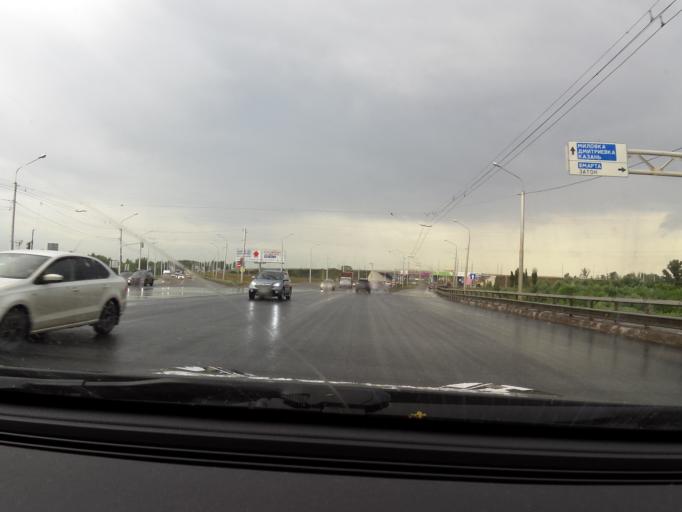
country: RU
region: Bashkortostan
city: Ufa
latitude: 54.7616
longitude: 55.9589
